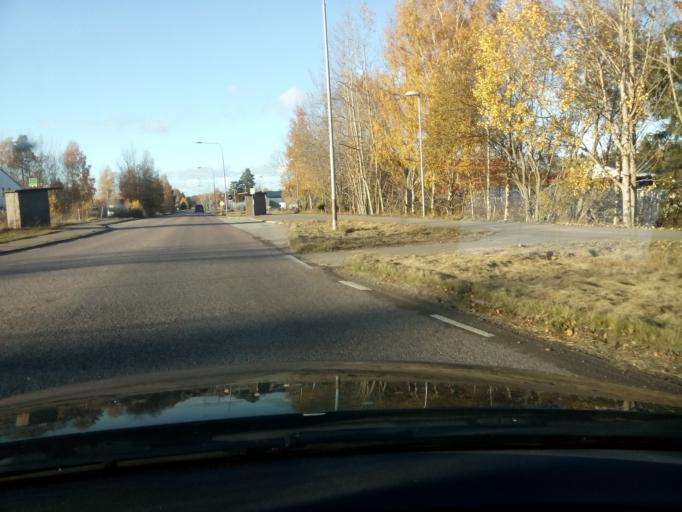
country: SE
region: Soedermanland
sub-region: Nykopings Kommun
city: Nykoping
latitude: 58.7178
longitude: 17.0281
